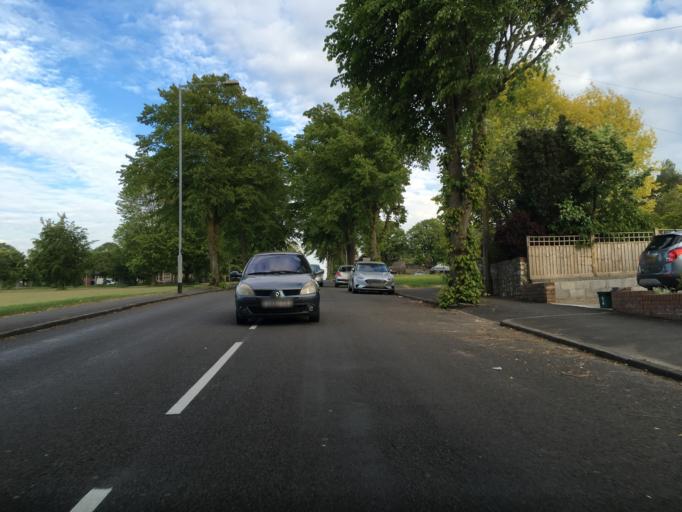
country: GB
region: England
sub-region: Bristol
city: Bristol
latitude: 51.4887
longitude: -2.5924
